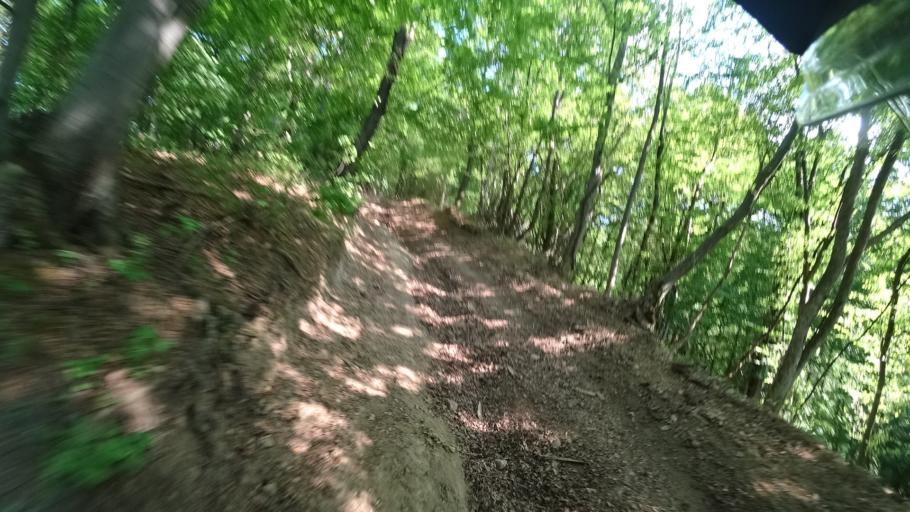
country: HR
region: Zagrebacka
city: Jablanovec
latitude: 45.8764
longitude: 15.8761
